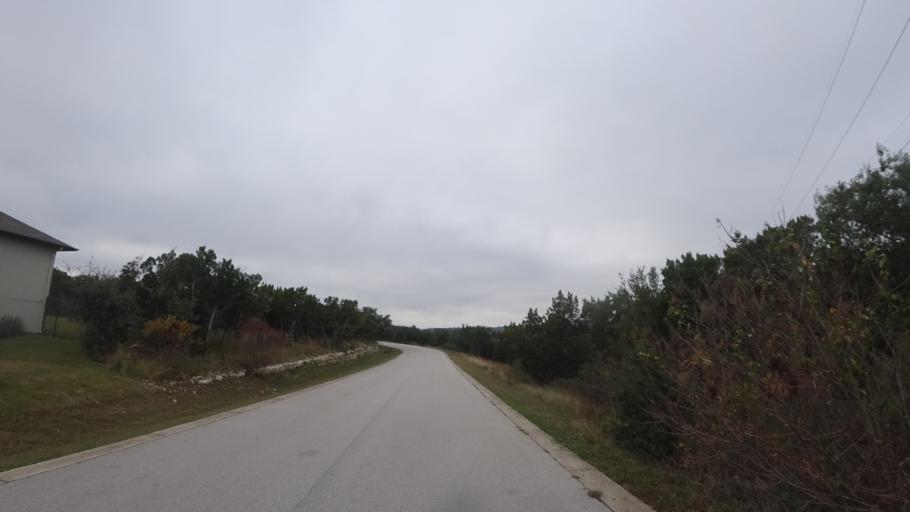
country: US
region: Texas
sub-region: Travis County
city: Hudson Bend
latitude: 30.3890
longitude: -97.9197
